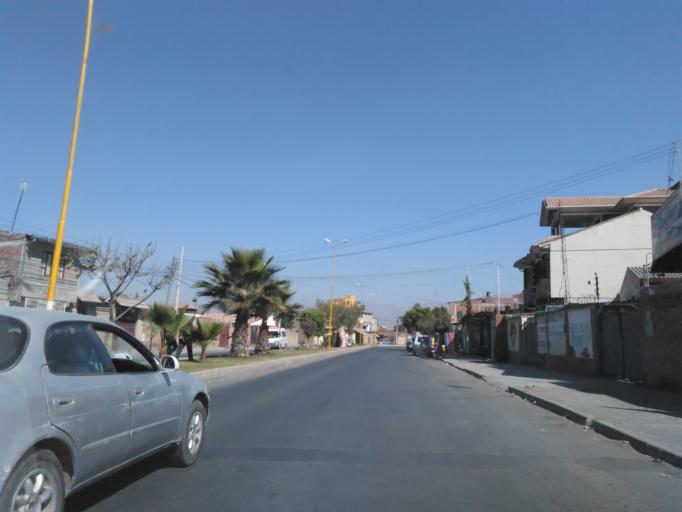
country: BO
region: Cochabamba
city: Cochabamba
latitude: -17.3945
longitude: -66.2709
